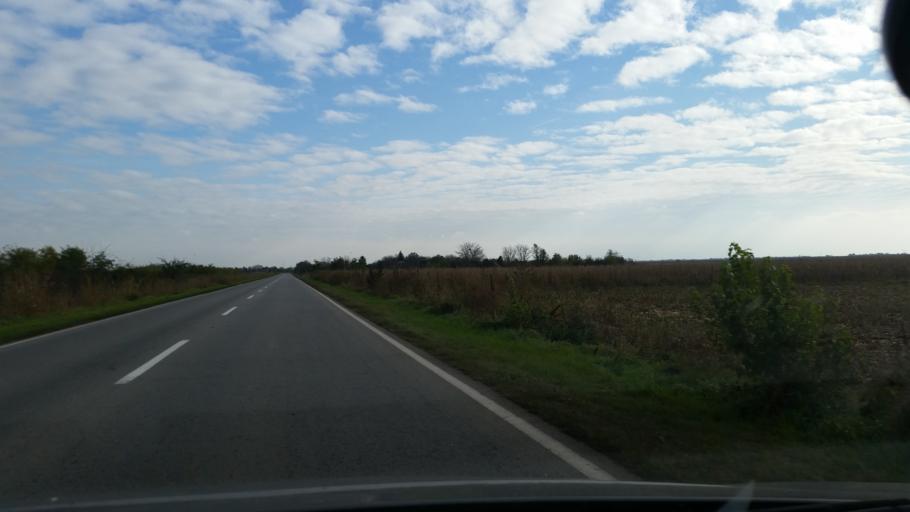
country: RS
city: Mihajlovo
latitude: 45.4420
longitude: 20.3621
